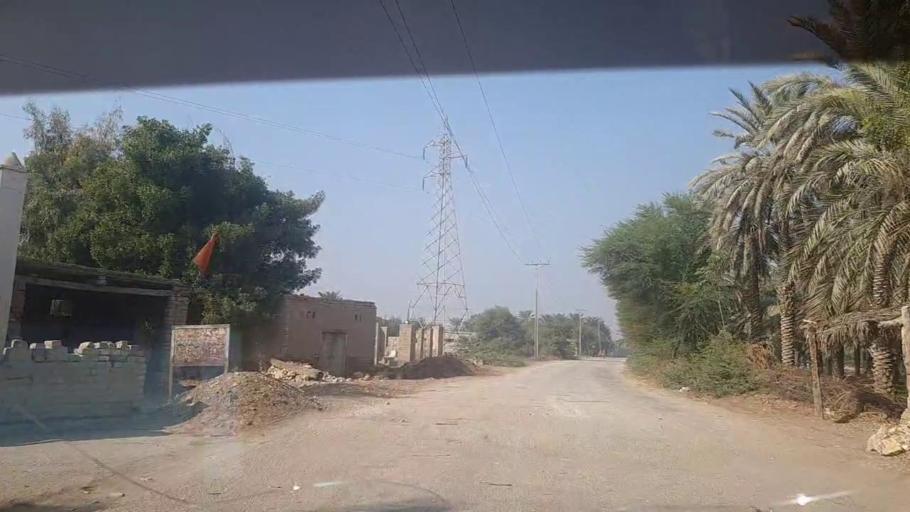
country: PK
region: Sindh
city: Kot Diji
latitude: 27.3649
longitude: 68.7038
